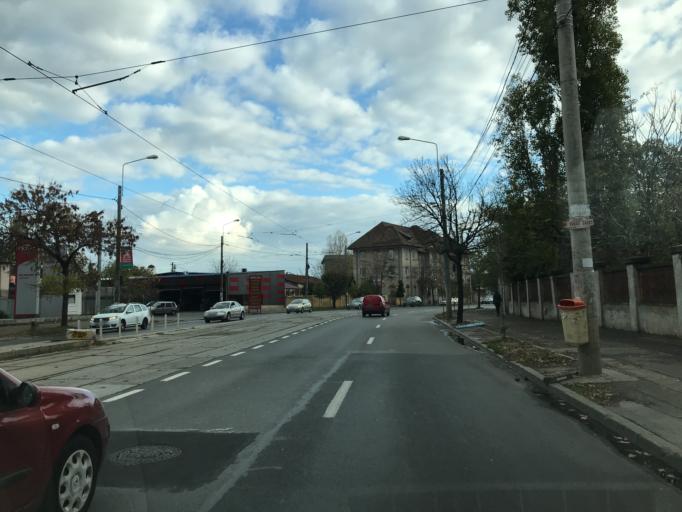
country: RO
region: Bucuresti
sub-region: Municipiul Bucuresti
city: Bucuresti
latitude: 44.4496
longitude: 26.0617
